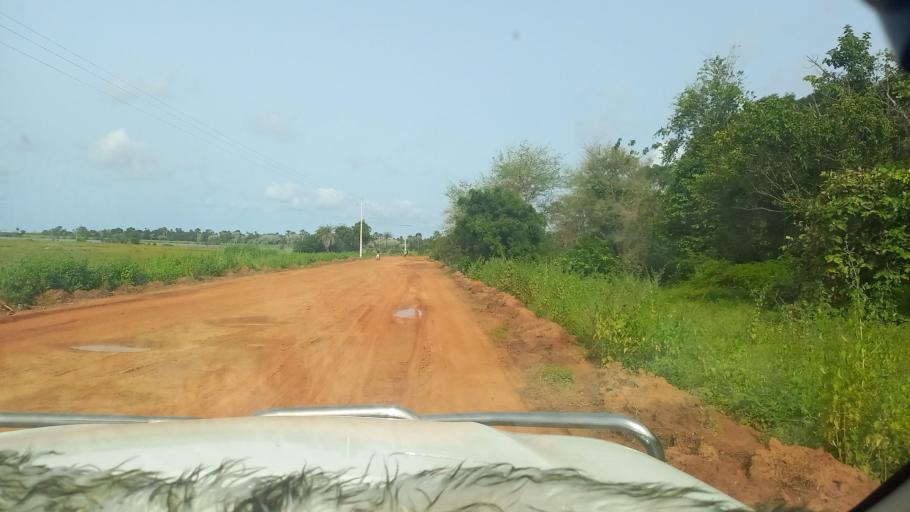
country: SN
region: Ziguinchor
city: Ziguinchor
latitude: 12.6710
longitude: -16.2774
